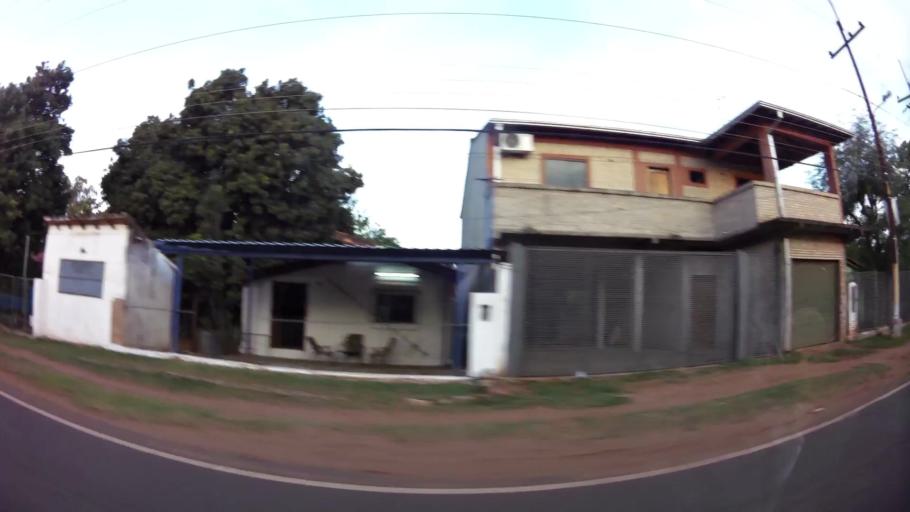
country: PY
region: Central
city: San Lorenzo
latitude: -25.3635
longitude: -57.4903
